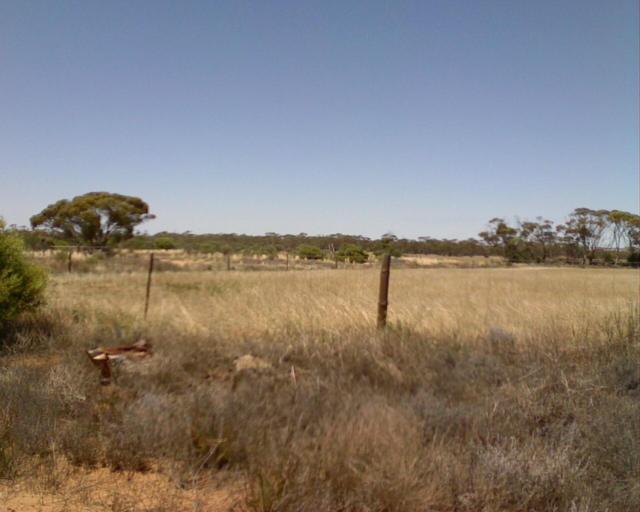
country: AU
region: South Australia
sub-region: Kimba
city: Caralue
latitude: -32.9474
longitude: 135.2831
